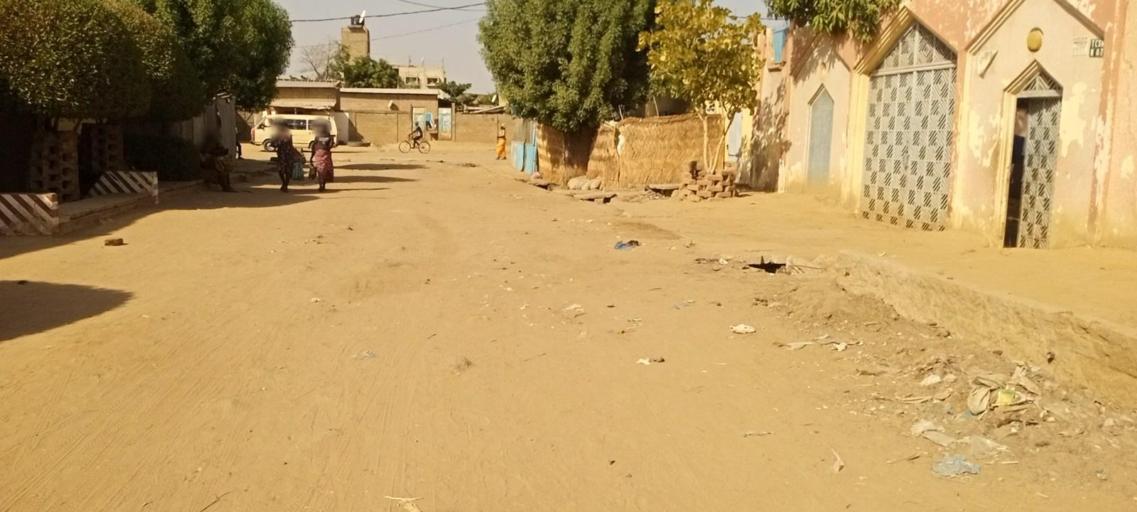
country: TD
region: Chari-Baguirmi
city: N'Djamena
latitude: 12.1126
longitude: 15.1141
